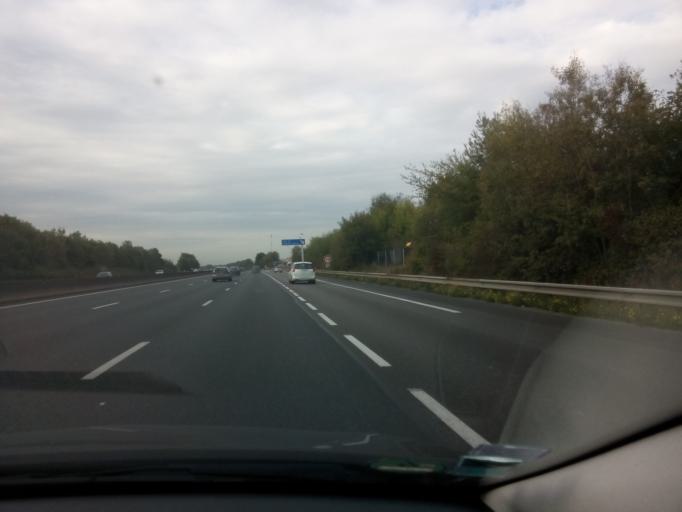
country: FR
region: Ile-de-France
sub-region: Departement de l'Essonne
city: Fontenay-les-Briis
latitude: 48.6389
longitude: 2.1532
